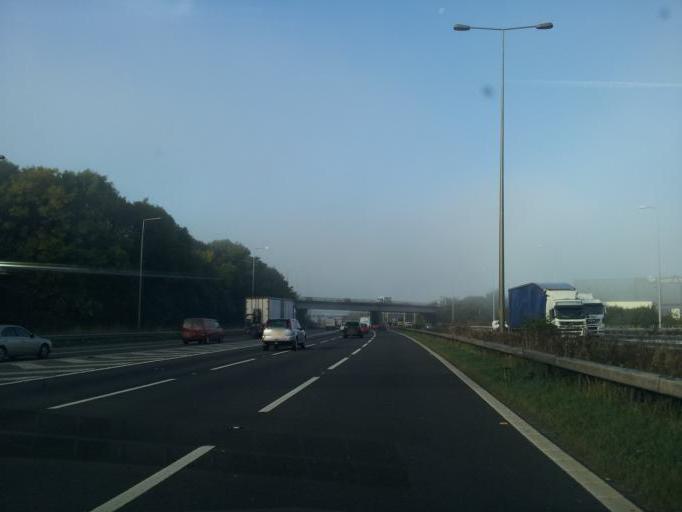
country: GB
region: England
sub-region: City and Borough of Leeds
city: Morley
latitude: 53.7330
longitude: -1.5825
